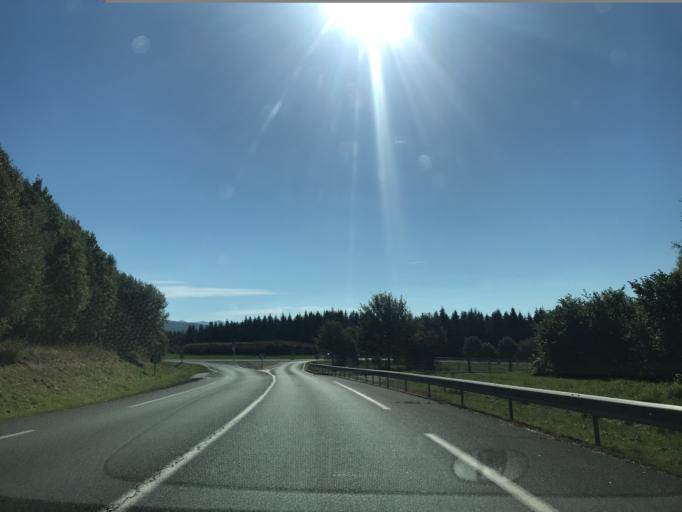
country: FR
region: Auvergne
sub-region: Departement du Puy-de-Dome
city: Saint-Sauves-d'Auvergne
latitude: 45.6570
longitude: 2.6885
